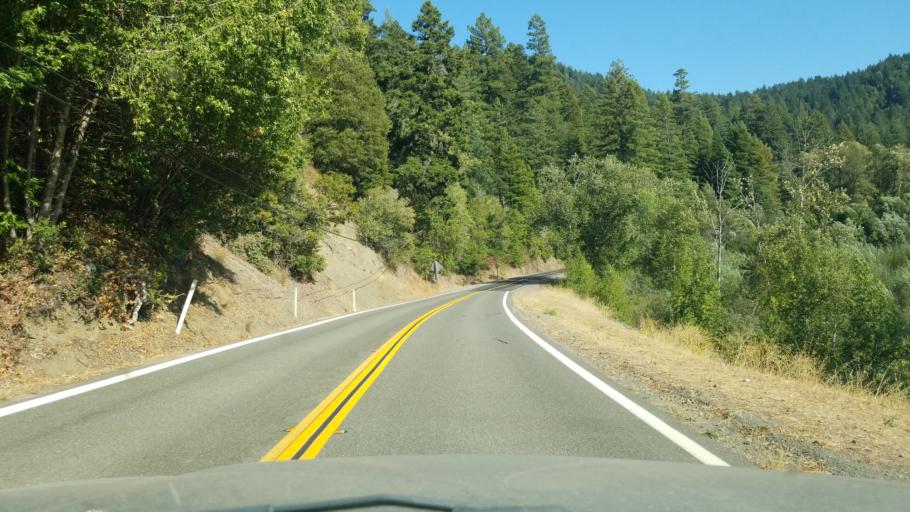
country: US
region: California
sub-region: Humboldt County
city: Redway
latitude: 40.2225
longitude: -123.7908
